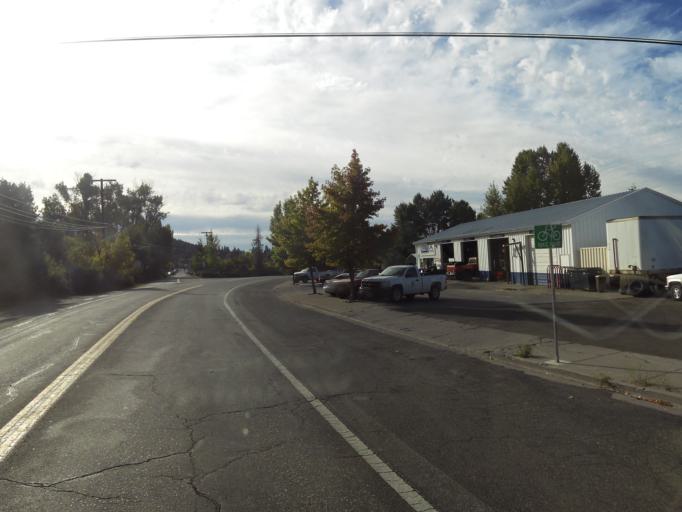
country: US
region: California
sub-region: Siskiyou County
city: Mount Shasta
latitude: 41.3194
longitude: -122.3189
